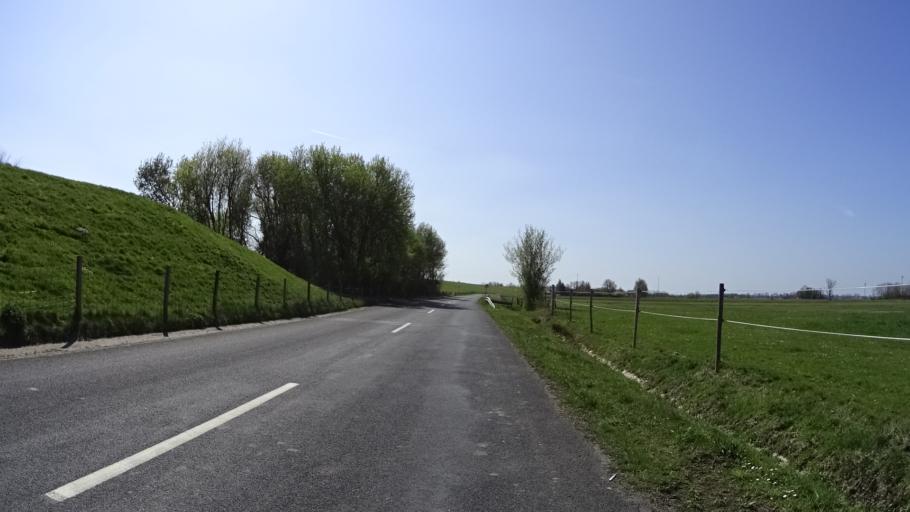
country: DE
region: Lower Saxony
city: Weener
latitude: 53.1990
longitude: 7.4038
